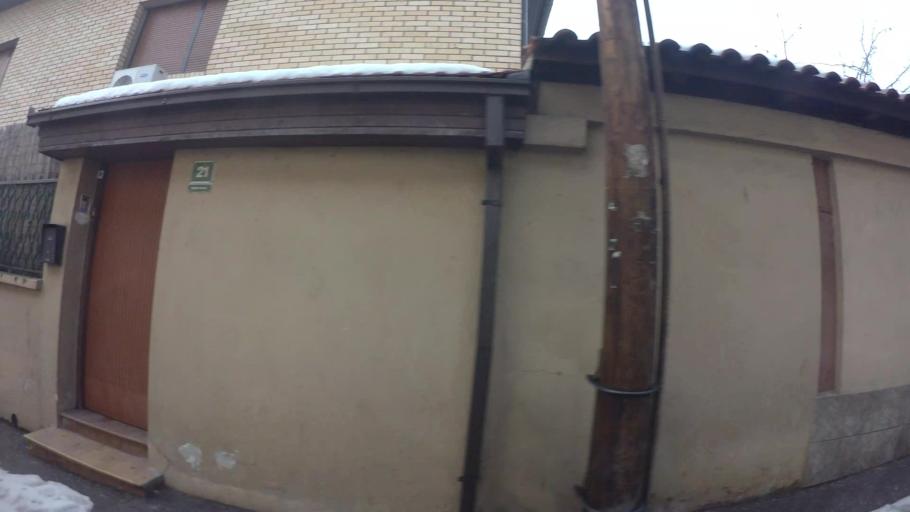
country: BA
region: Federation of Bosnia and Herzegovina
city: Kobilja Glava
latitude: 43.8620
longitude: 18.4241
